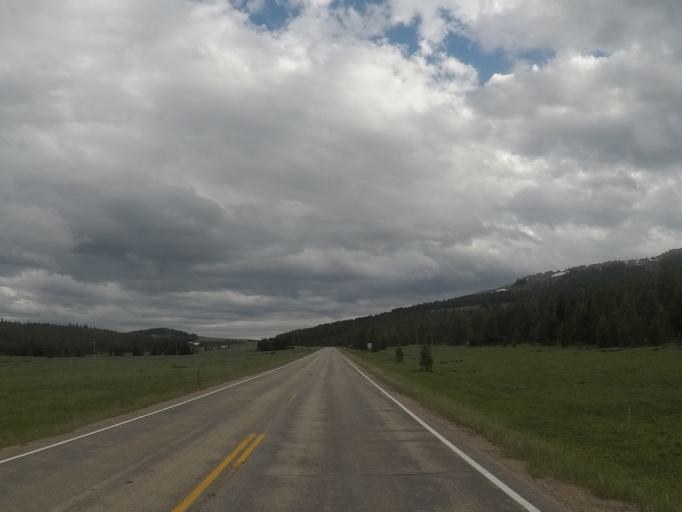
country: US
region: Wyoming
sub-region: Sheridan County
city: Sheridan
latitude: 44.6693
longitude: -107.4931
